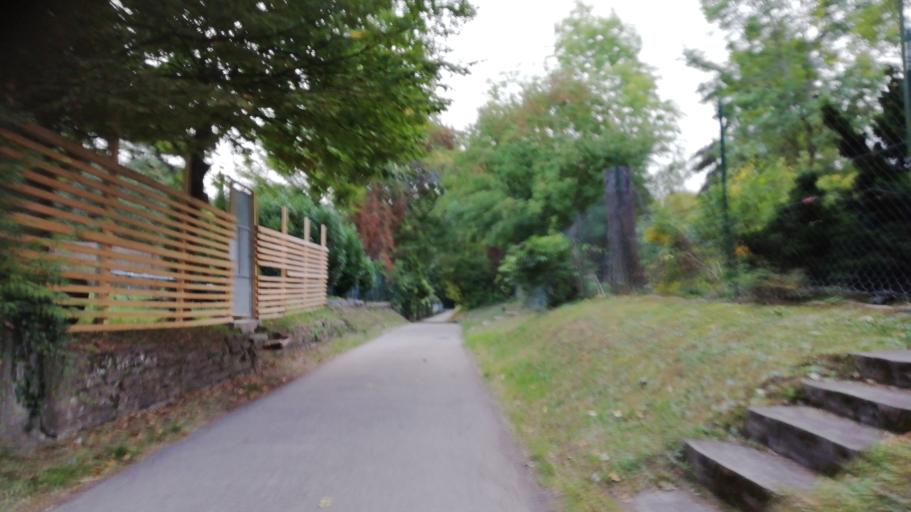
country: DE
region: Baden-Wuerttemberg
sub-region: Regierungsbezirk Stuttgart
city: Korntal
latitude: 48.8187
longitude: 9.1284
